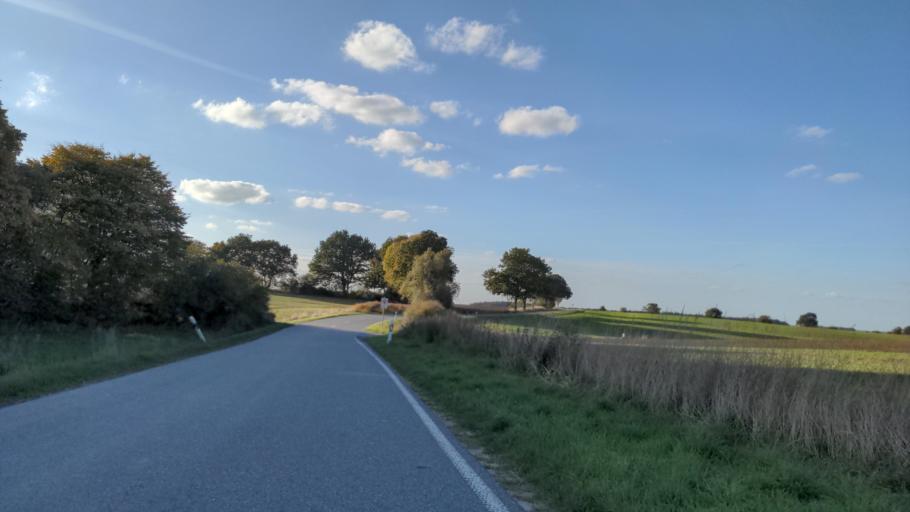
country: DE
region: Schleswig-Holstein
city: Pronstorf
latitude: 53.9610
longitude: 10.5179
